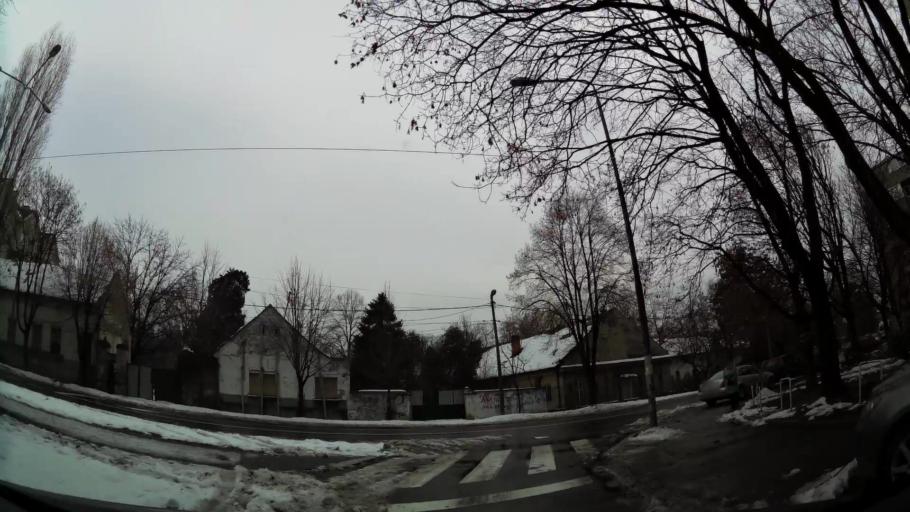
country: RS
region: Central Serbia
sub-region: Belgrade
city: Zemun
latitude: 44.8434
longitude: 20.3990
